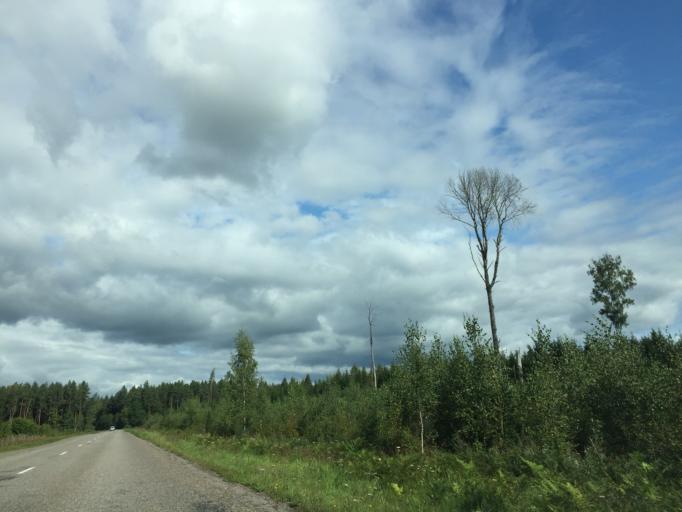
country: LV
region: Pargaujas
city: Stalbe
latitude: 57.4409
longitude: 24.9261
